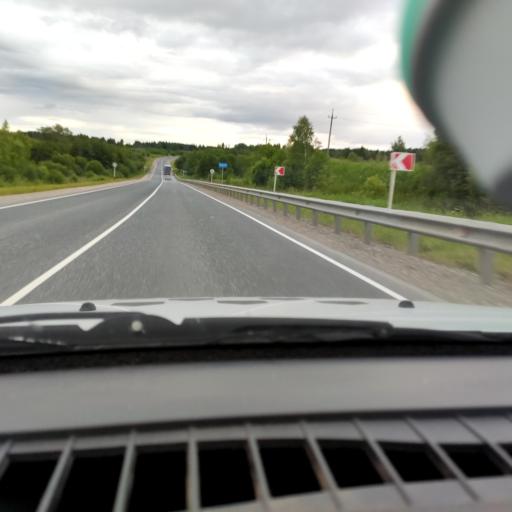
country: RU
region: Perm
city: Kalino
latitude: 58.2848
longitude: 57.4156
